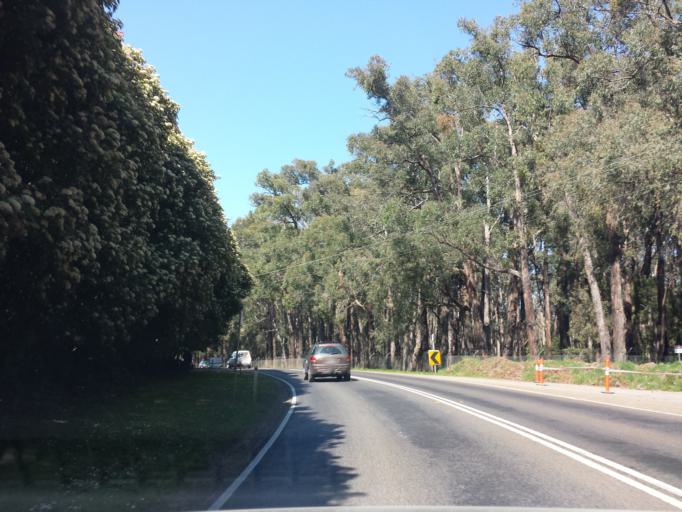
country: AU
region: Victoria
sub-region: Yarra Ranges
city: Monbulk
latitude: -37.8466
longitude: 145.4225
